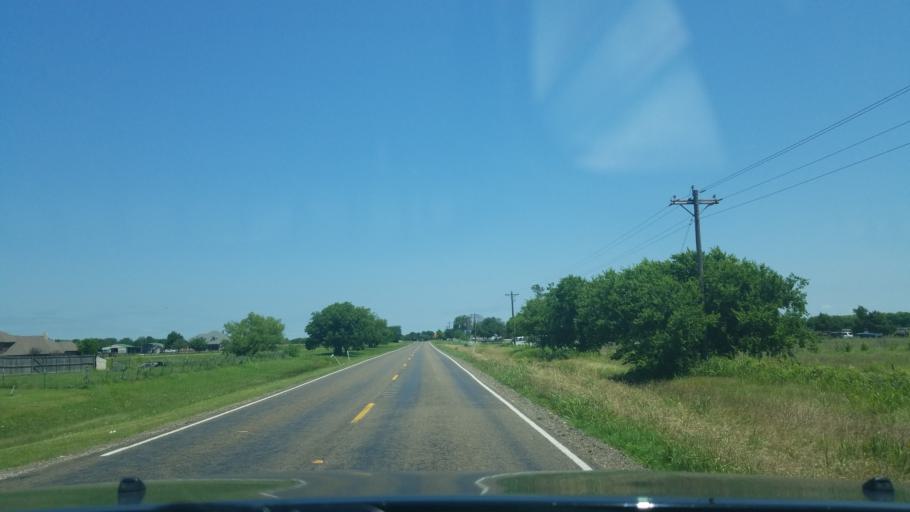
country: US
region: Texas
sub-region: Denton County
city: Krum
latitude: 33.3102
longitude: -97.2373
